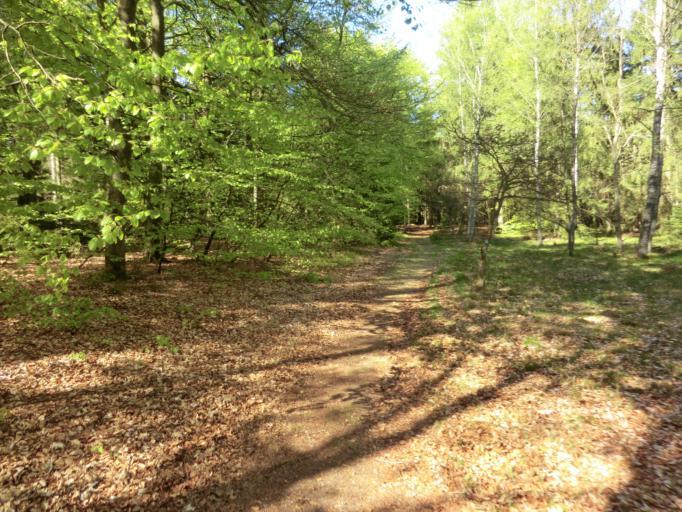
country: SE
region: Skane
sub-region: Sjobo Kommun
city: Sjoebo
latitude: 55.5733
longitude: 13.7146
